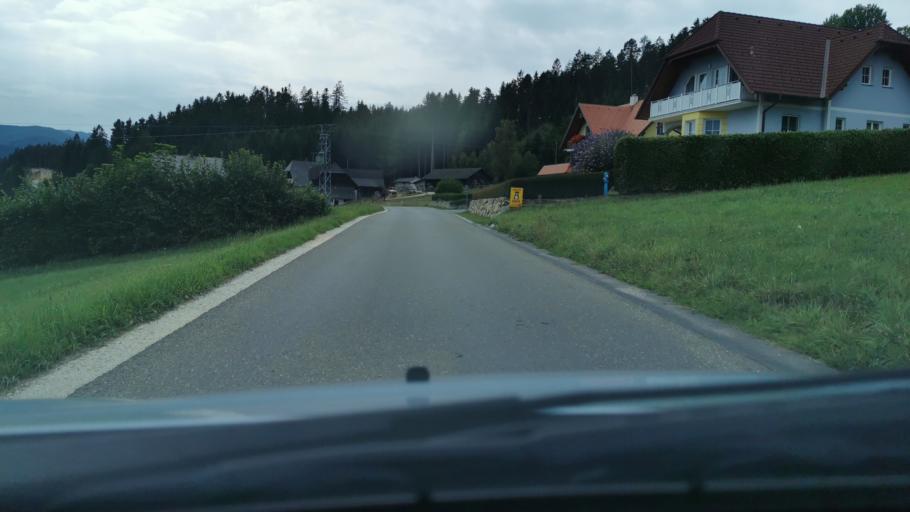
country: AT
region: Styria
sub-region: Politischer Bezirk Weiz
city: Strallegg
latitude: 47.3943
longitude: 15.6786
